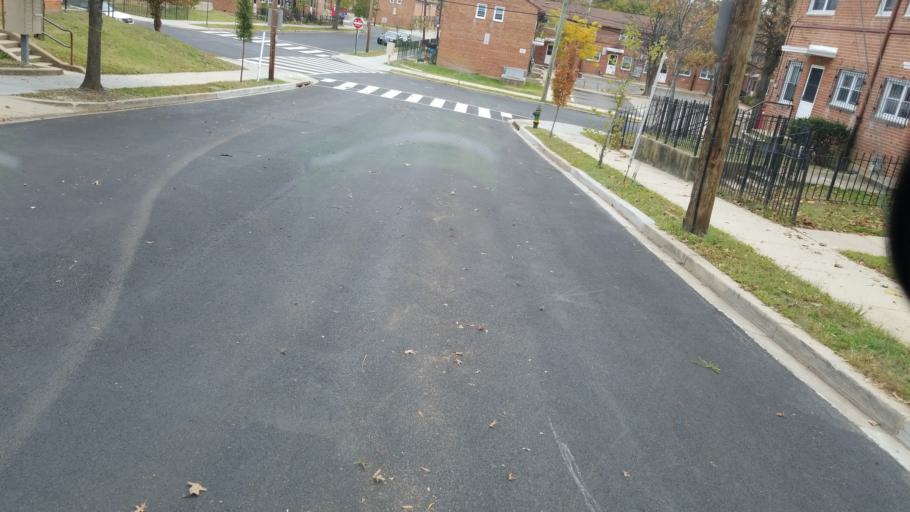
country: US
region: Maryland
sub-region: Prince George's County
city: Fairmount Heights
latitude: 38.8935
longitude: -76.9259
